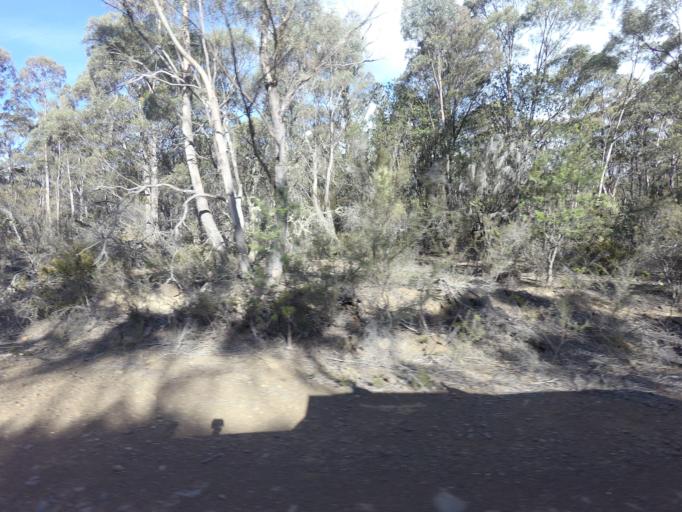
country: AU
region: Tasmania
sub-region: Break O'Day
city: St Helens
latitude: -41.8572
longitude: 148.0247
